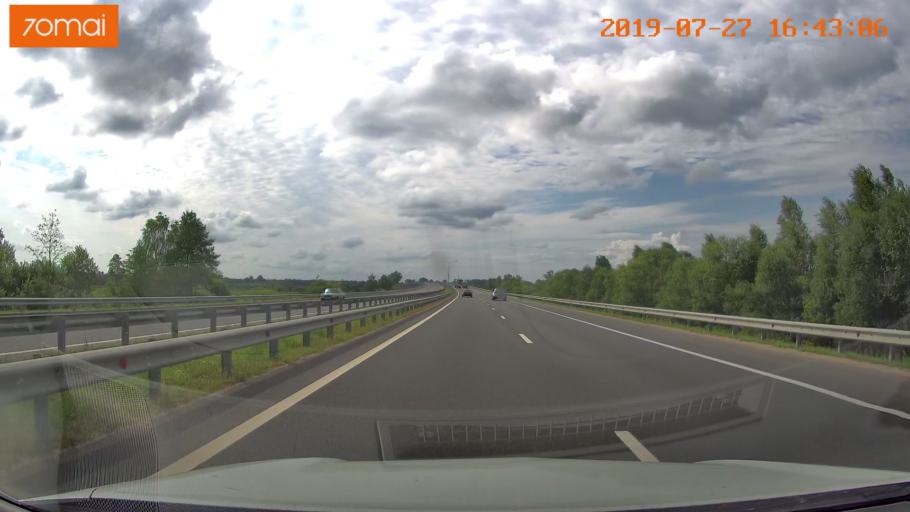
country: RU
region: Kaliningrad
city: Gvardeysk
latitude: 54.6696
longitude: 21.1111
